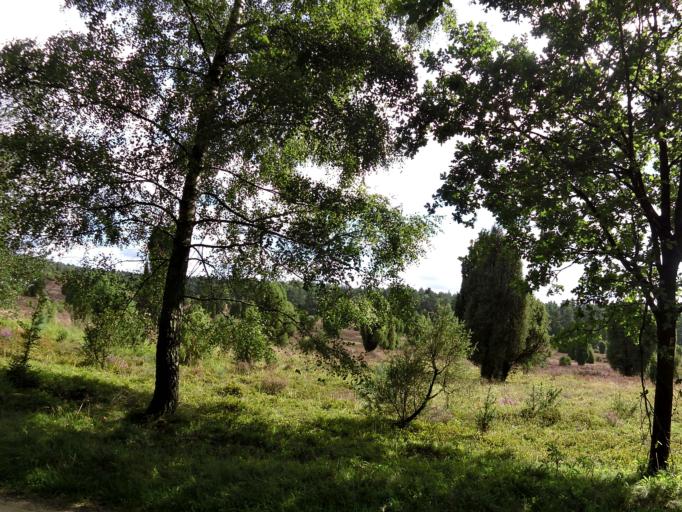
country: DE
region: Lower Saxony
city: Undeloh
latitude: 53.1483
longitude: 9.9561
